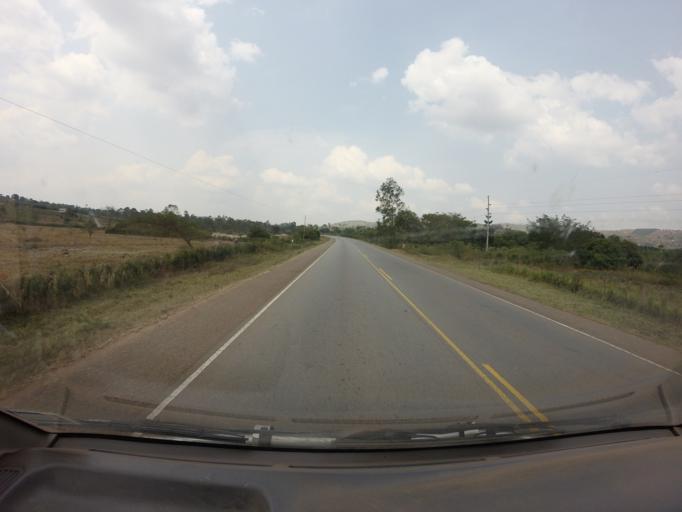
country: UG
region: Central Region
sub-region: Lyantonde District
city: Lyantonde
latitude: -0.3842
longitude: 31.2231
